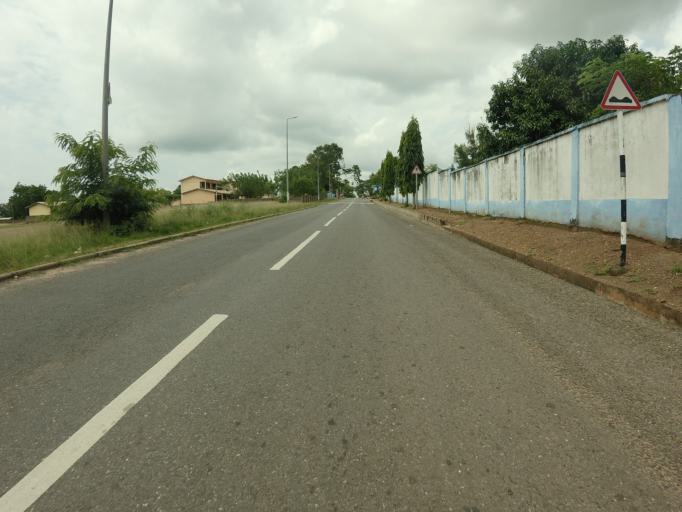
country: GH
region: Volta
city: Ho
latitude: 6.6013
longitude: 0.4733
